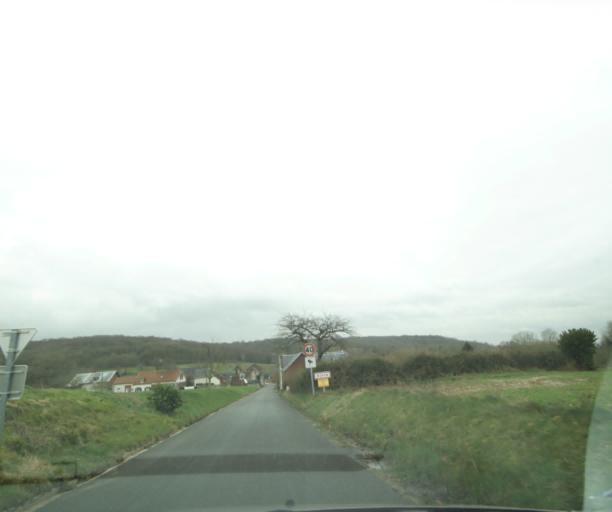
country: FR
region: Picardie
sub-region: Departement de l'Oise
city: Noyon
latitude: 49.6001
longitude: 3.0135
